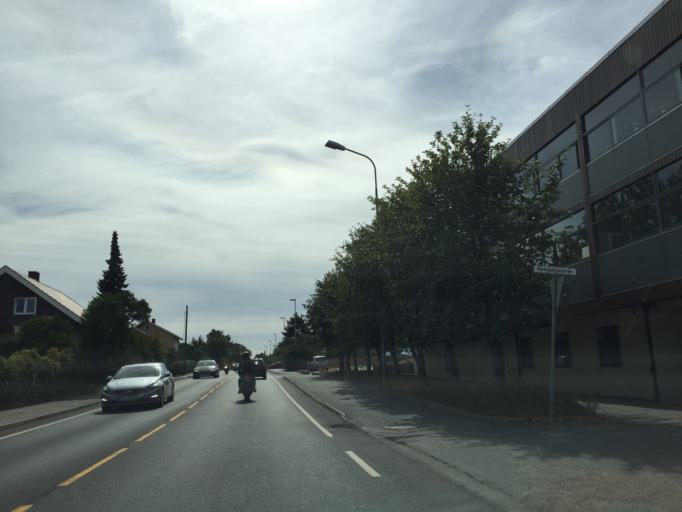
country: NO
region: Ostfold
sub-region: Fredrikstad
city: Fredrikstad
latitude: 59.2015
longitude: 10.9391
